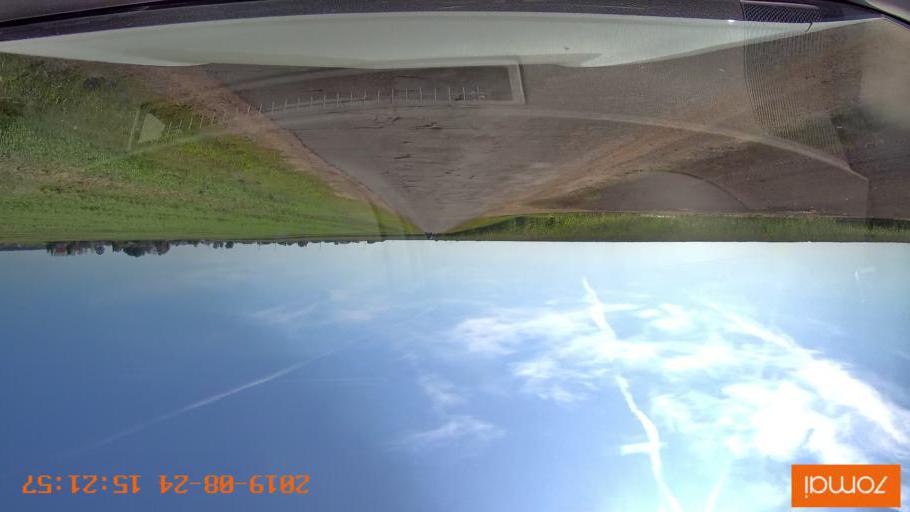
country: BY
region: Minsk
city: Samakhvalavichy
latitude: 53.6768
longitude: 27.5094
